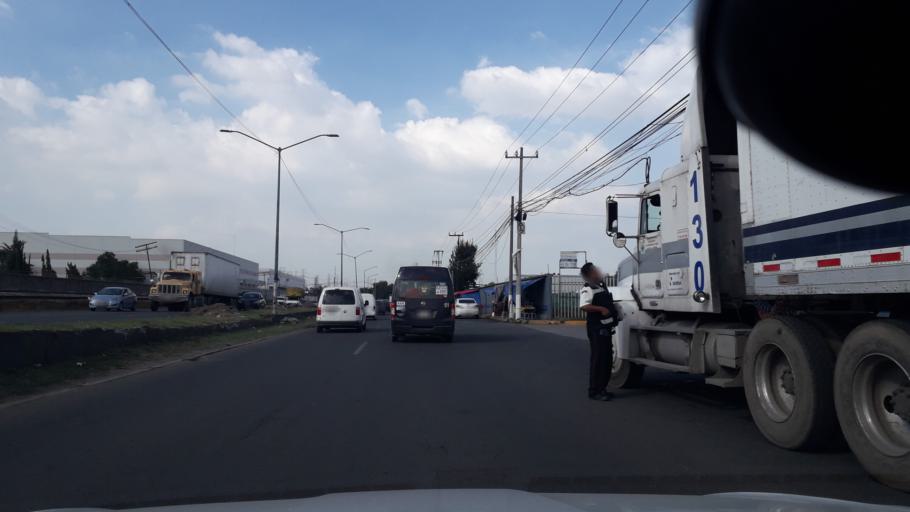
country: MX
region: Mexico
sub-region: Tultitlan
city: Buenavista
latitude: 19.6278
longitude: -99.1848
